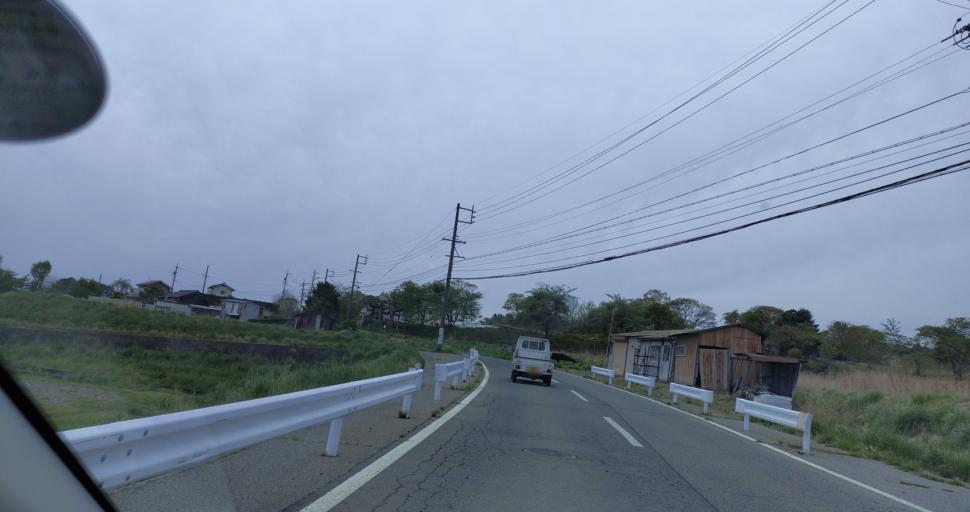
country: JP
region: Nagano
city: Komoro
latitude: 36.3362
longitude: 138.4866
